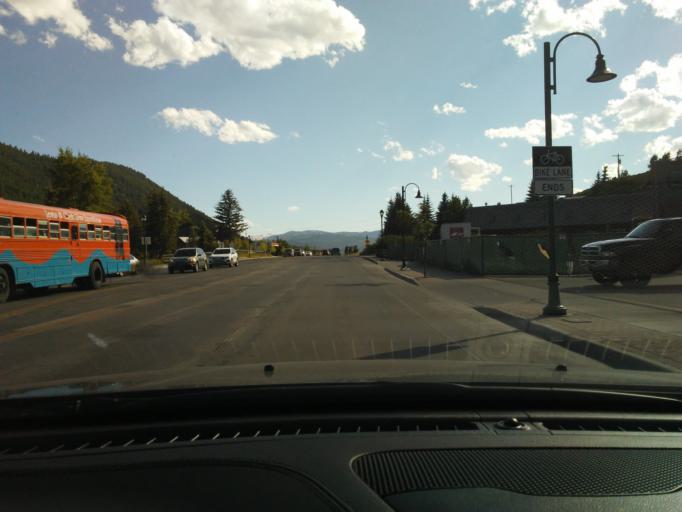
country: US
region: Wyoming
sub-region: Teton County
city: Jackson
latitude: 43.4783
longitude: -110.7706
